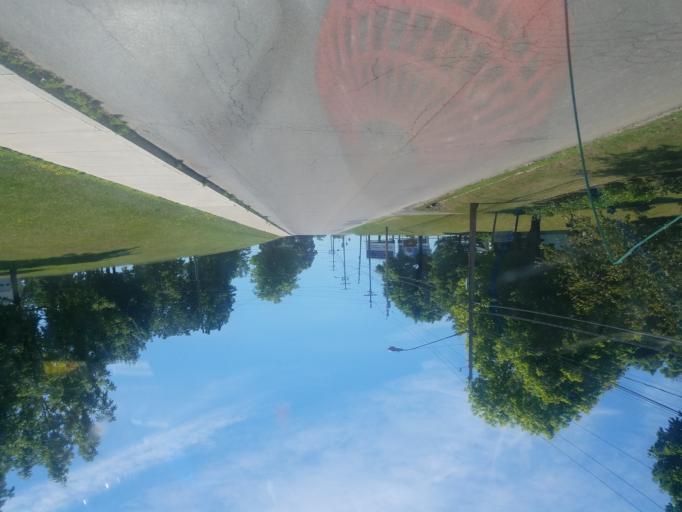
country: US
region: New York
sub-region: Yates County
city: Penn Yan
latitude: 42.6538
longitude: -77.0424
